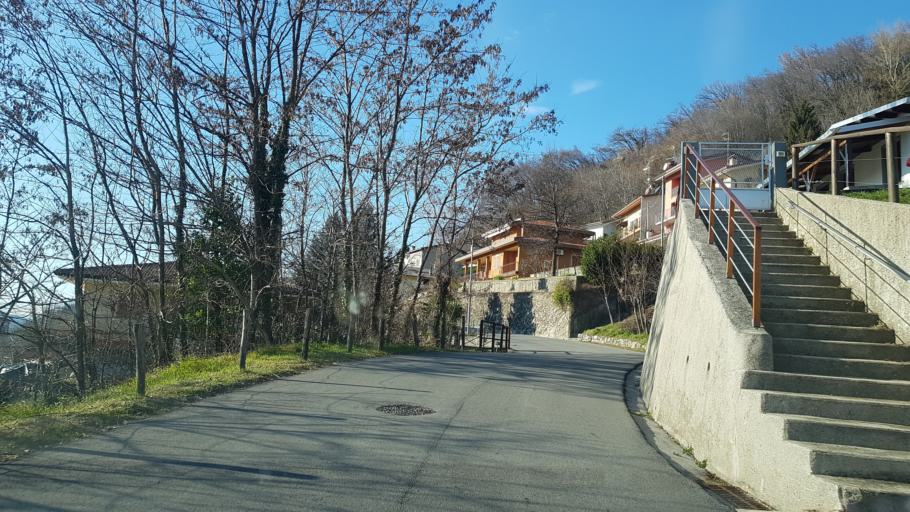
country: IT
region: Friuli Venezia Giulia
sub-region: Provincia di Udine
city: Forgaria nel Friuli
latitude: 46.2247
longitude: 12.9723
